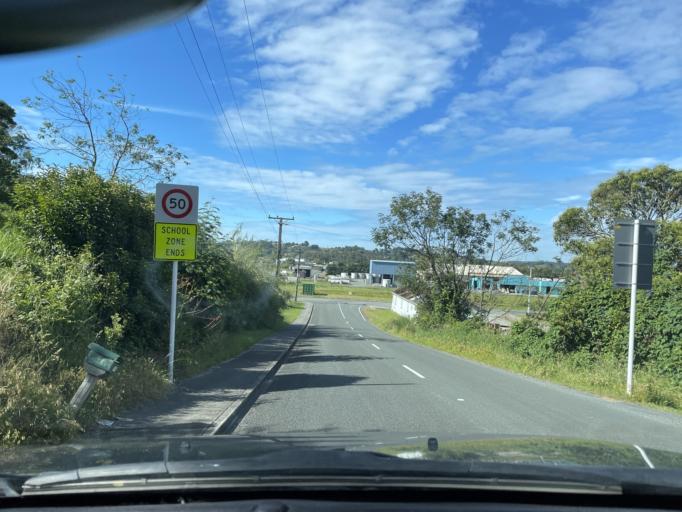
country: NZ
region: Northland
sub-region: Kaipara District
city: Dargaville
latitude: -35.9394
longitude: 173.8643
